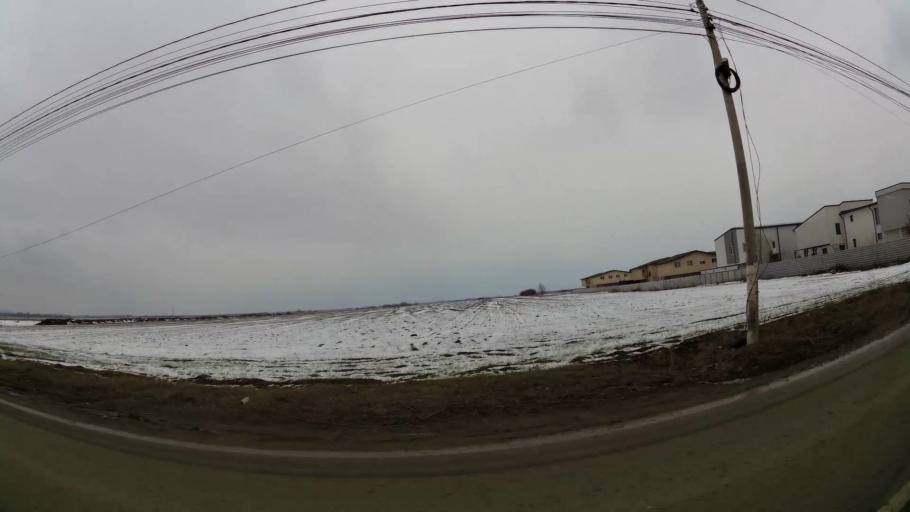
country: RO
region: Ilfov
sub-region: Comuna Tunari
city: Tunari
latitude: 44.5503
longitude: 26.1192
